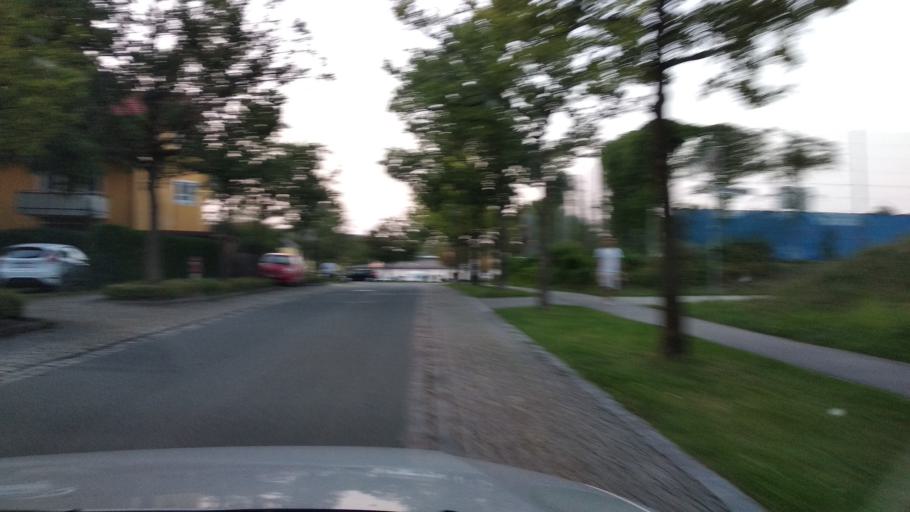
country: DE
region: Bavaria
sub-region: Upper Bavaria
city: Ebersberg
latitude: 48.0750
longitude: 11.9556
